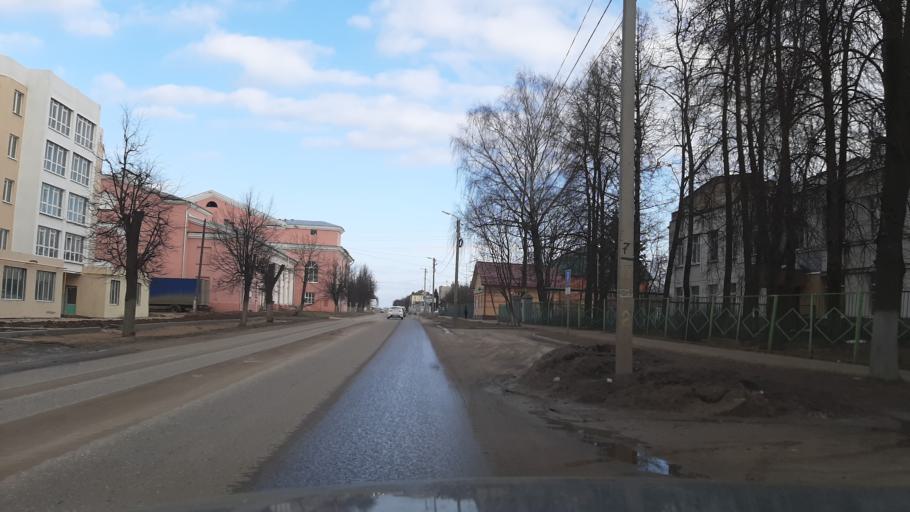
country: RU
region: Ivanovo
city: Teykovo
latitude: 56.8544
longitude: 40.5311
